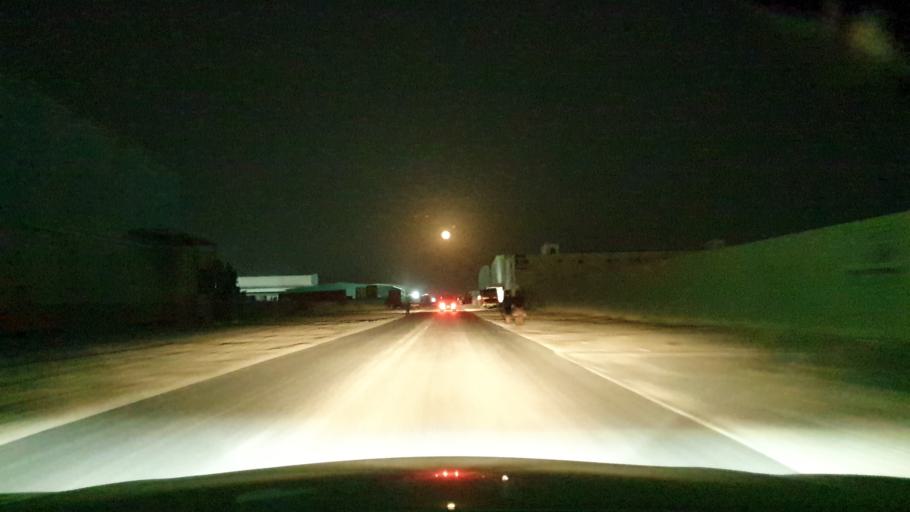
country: BH
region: Northern
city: Sitrah
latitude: 26.0973
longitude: 50.6177
